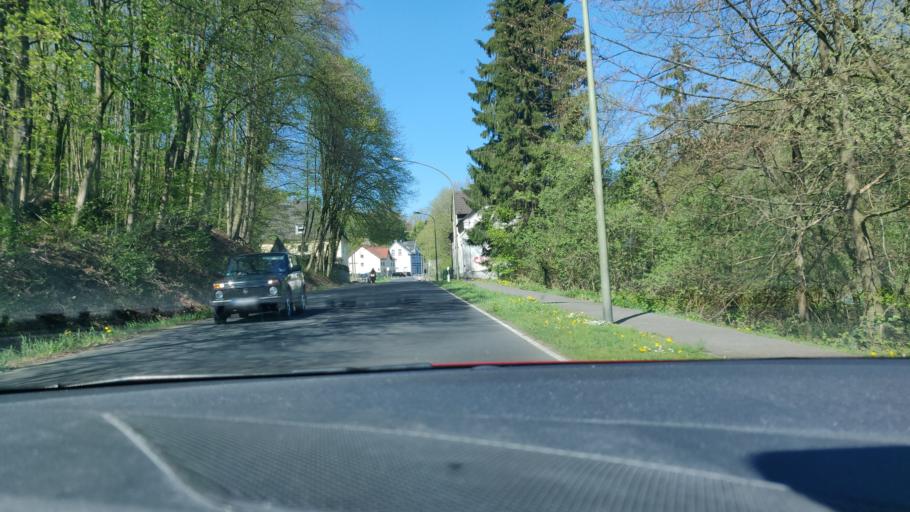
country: DE
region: North Rhine-Westphalia
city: Wulfrath
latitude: 51.2864
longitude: 7.0672
